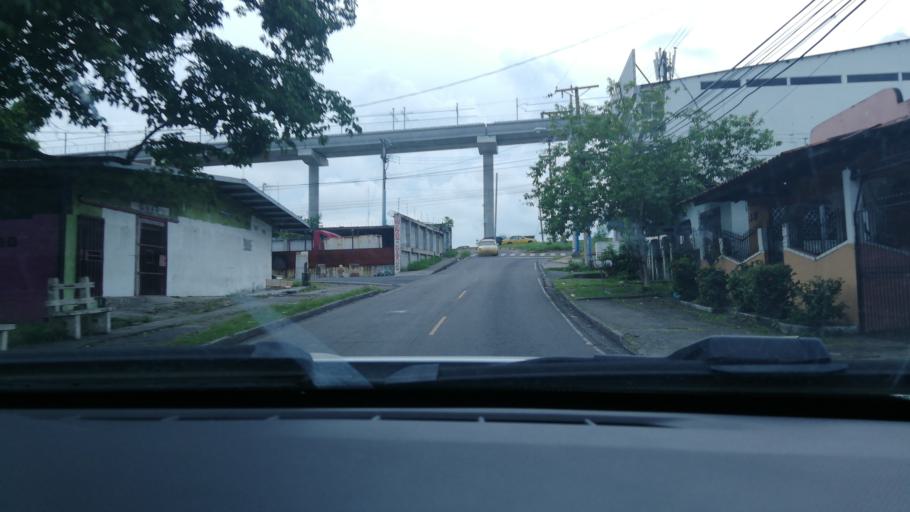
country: PA
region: Panama
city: San Miguelito
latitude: 9.0340
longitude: -79.4880
